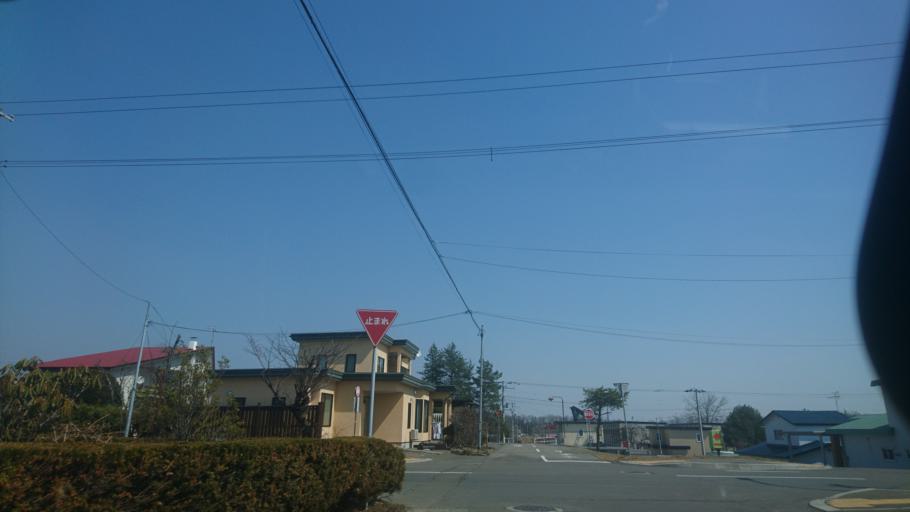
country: JP
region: Hokkaido
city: Obihiro
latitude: 42.9127
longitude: 143.0587
